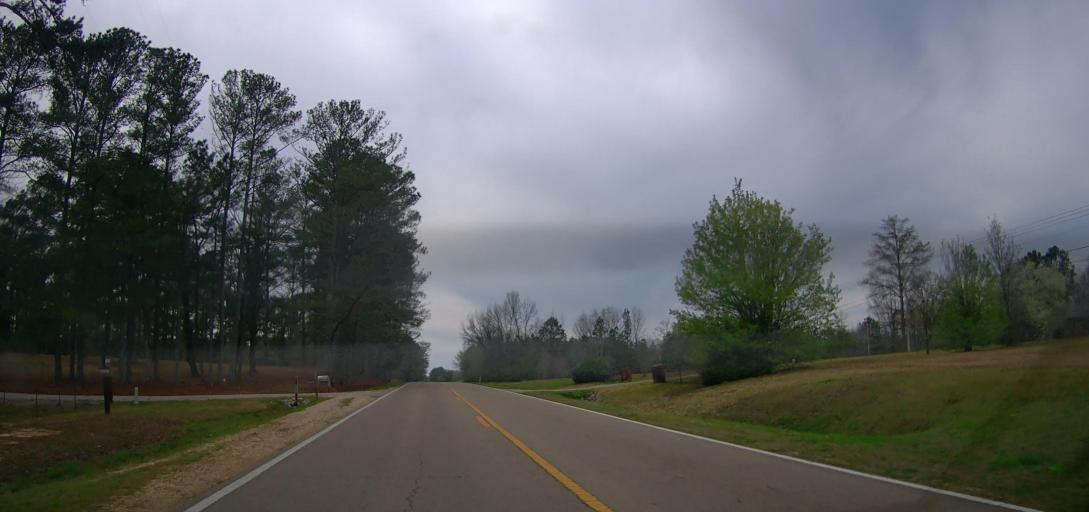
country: US
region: Mississippi
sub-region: Itawamba County
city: Mantachie
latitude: 34.2637
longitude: -88.5387
